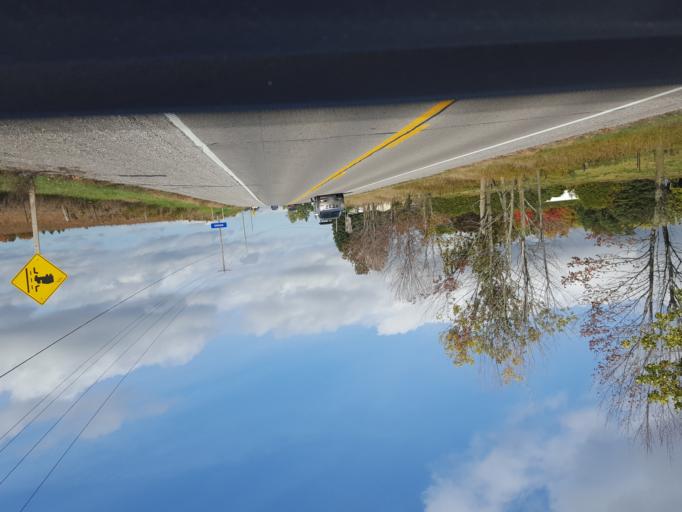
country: CA
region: Ontario
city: Oshawa
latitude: 43.9893
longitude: -78.6284
